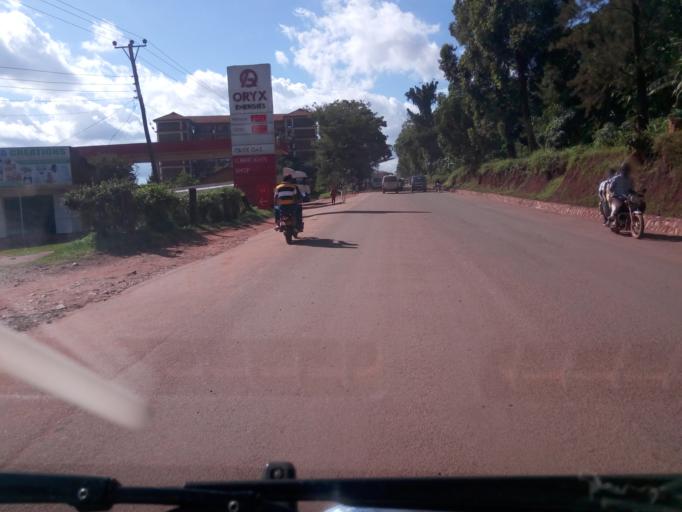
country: UG
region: Central Region
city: Kampala Central Division
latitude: 0.3330
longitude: 32.5642
